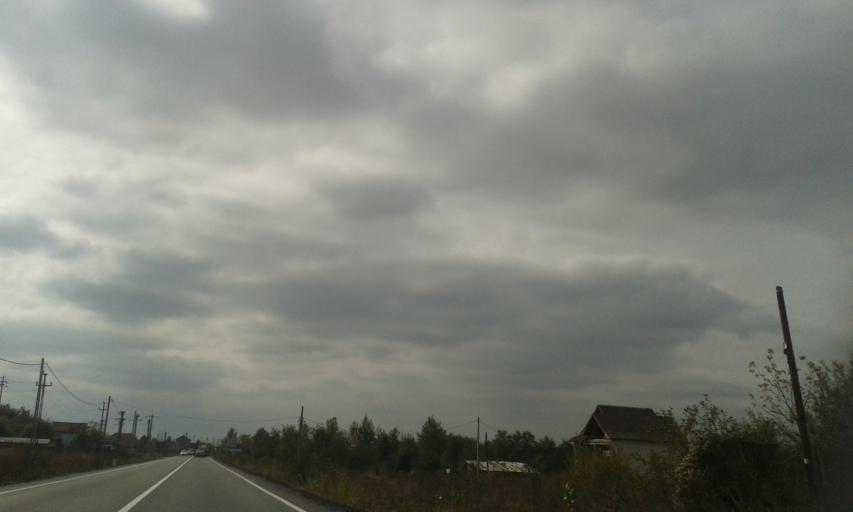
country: RO
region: Gorj
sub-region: Comuna Turcinesti
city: Turcinesti
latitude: 45.1044
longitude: 23.3384
